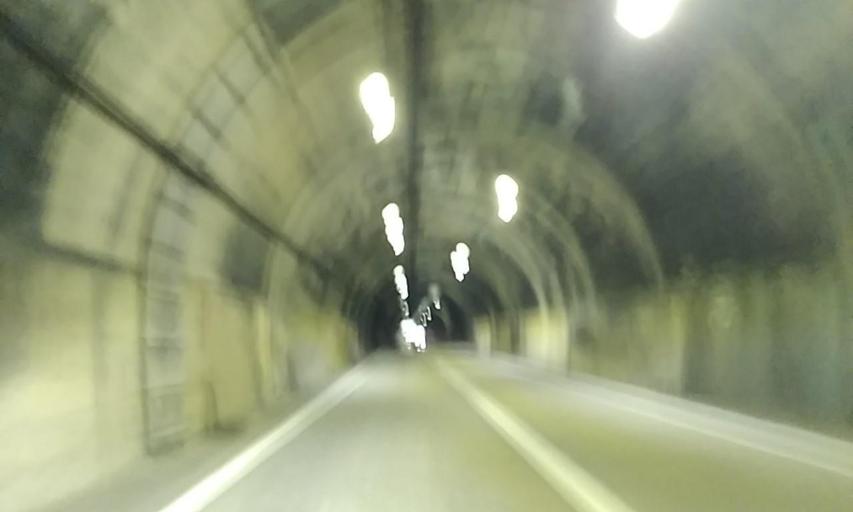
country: JP
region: Mie
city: Ise
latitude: 34.4112
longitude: 136.7644
